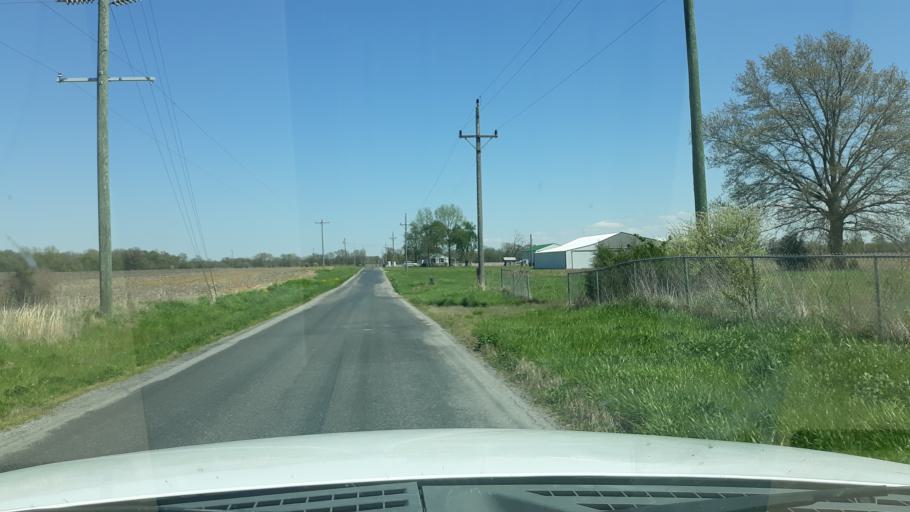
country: US
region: Illinois
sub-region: Saline County
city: Harrisburg
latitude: 37.8342
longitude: -88.6387
